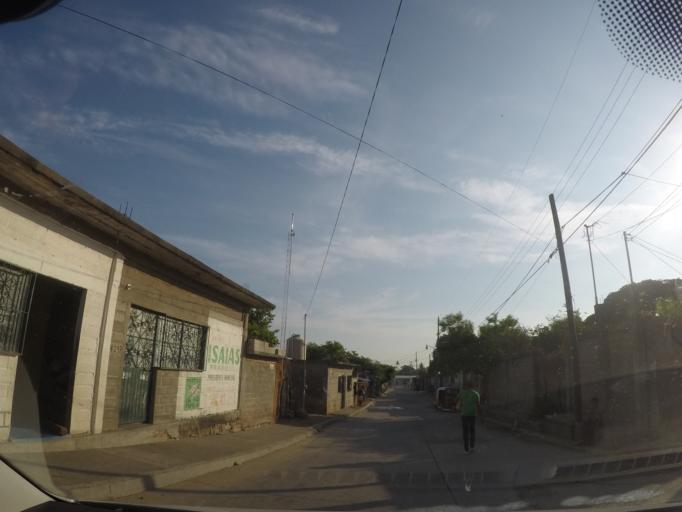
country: MX
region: Oaxaca
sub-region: Santo Domingo Tehuantepec
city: La Noria
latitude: 16.2451
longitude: -95.1498
